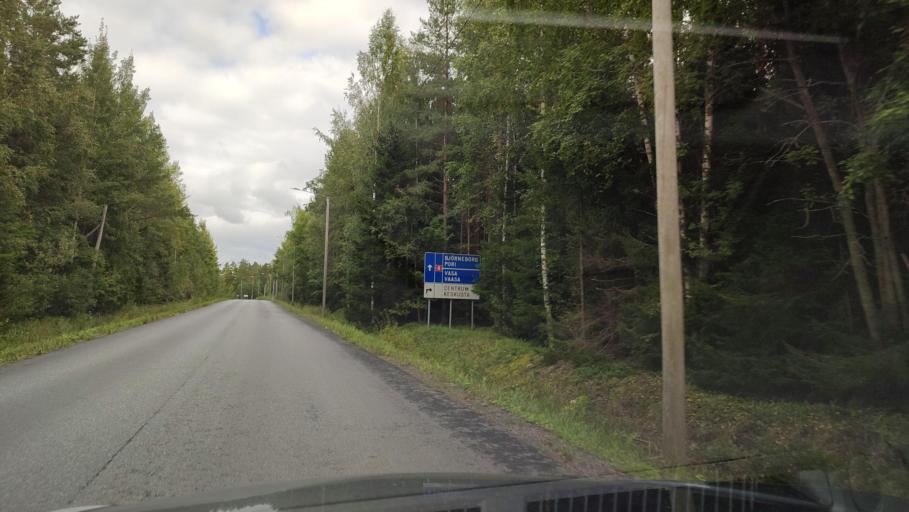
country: FI
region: Ostrobothnia
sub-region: Sydosterbotten
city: Kristinestad
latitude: 62.2597
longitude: 21.3474
